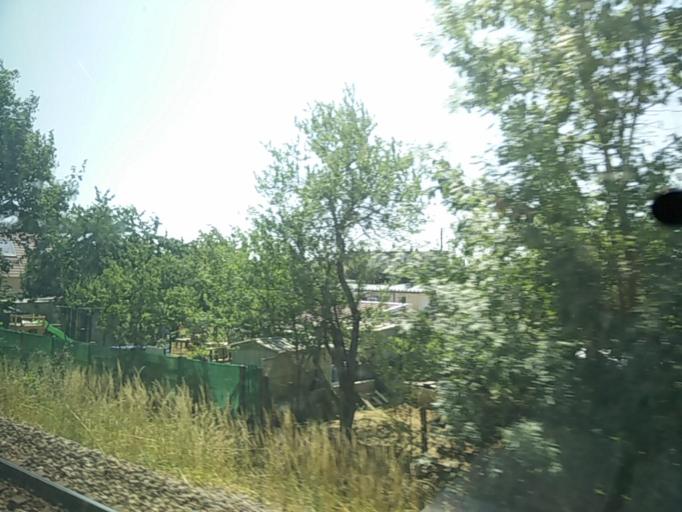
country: FR
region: Ile-de-France
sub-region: Departement de Seine-et-Marne
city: Nangis
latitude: 48.5589
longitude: 3.0196
